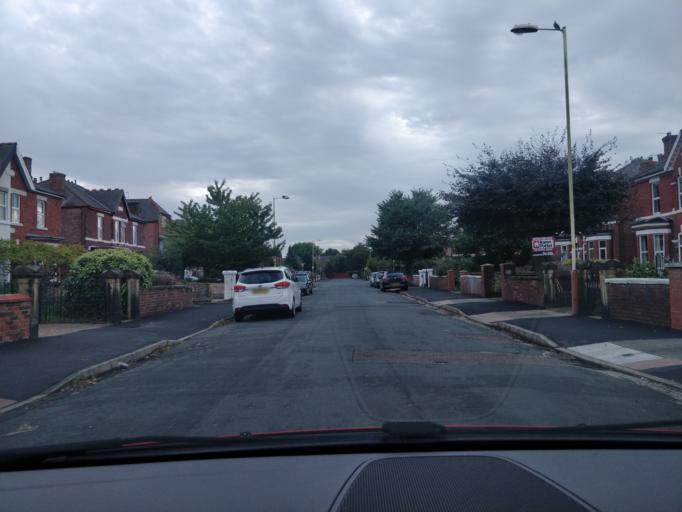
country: GB
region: England
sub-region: Sefton
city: Southport
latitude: 53.6433
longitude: -2.9827
